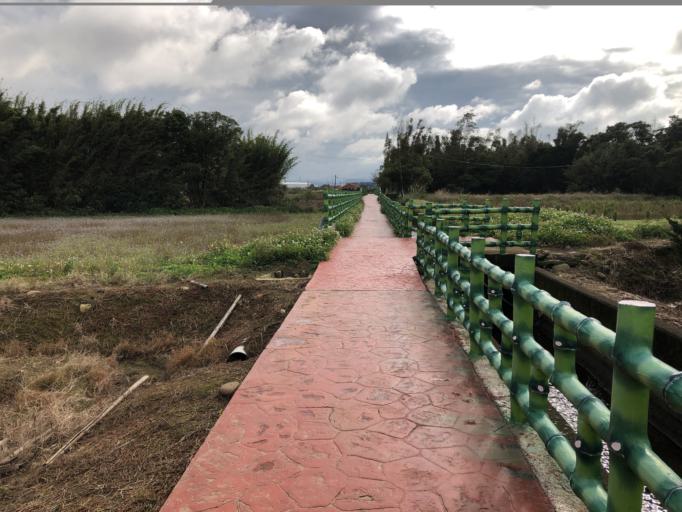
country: TW
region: Taiwan
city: Daxi
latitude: 24.9166
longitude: 121.2609
